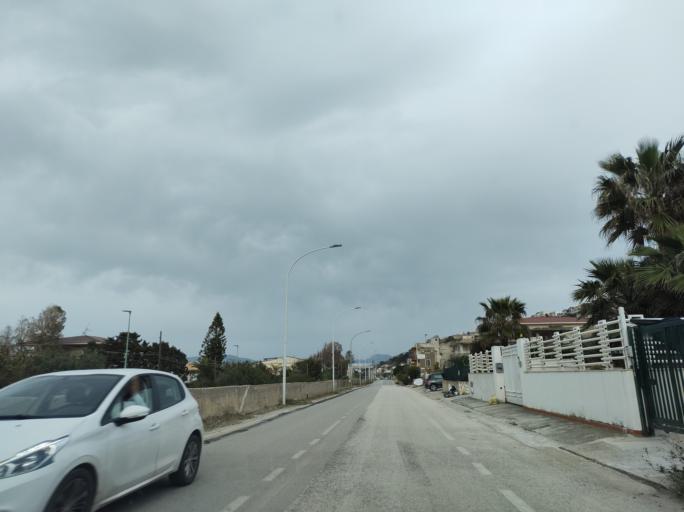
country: IT
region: Sicily
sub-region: Trapani
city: Alcamo
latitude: 38.0259
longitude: 12.9255
